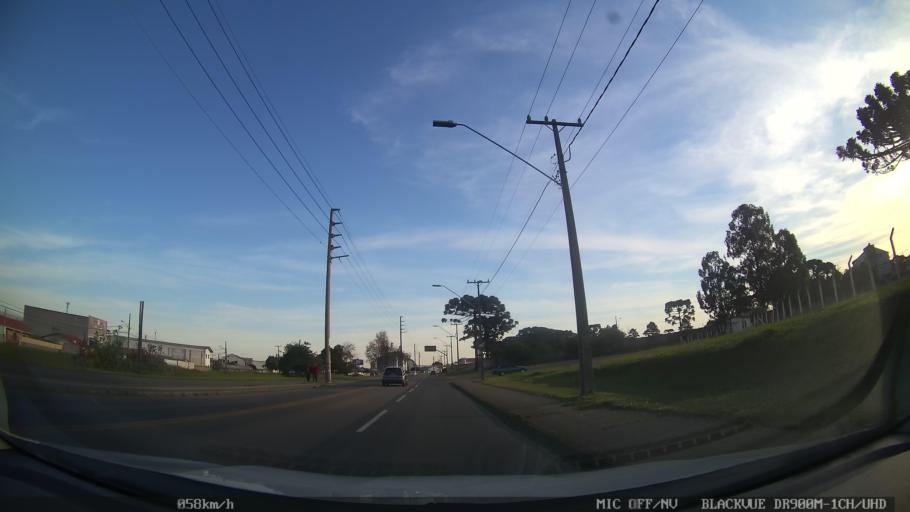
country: BR
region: Parana
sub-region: Pinhais
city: Pinhais
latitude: -25.4433
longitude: -49.1846
